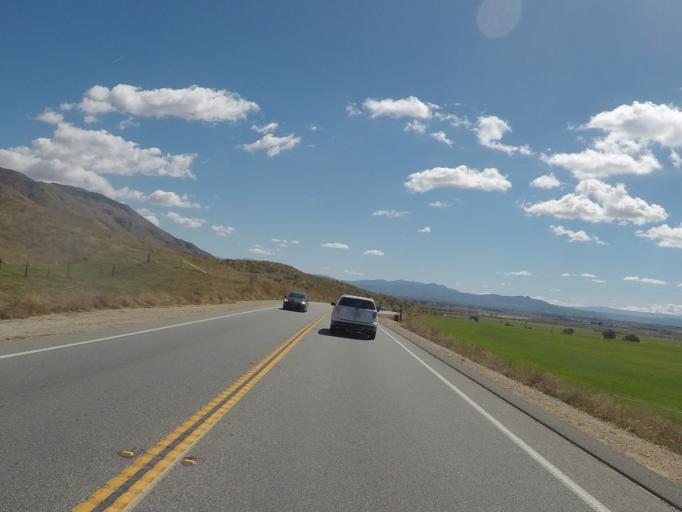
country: US
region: California
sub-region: Riverside County
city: Beaumont
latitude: 33.8516
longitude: -117.0132
